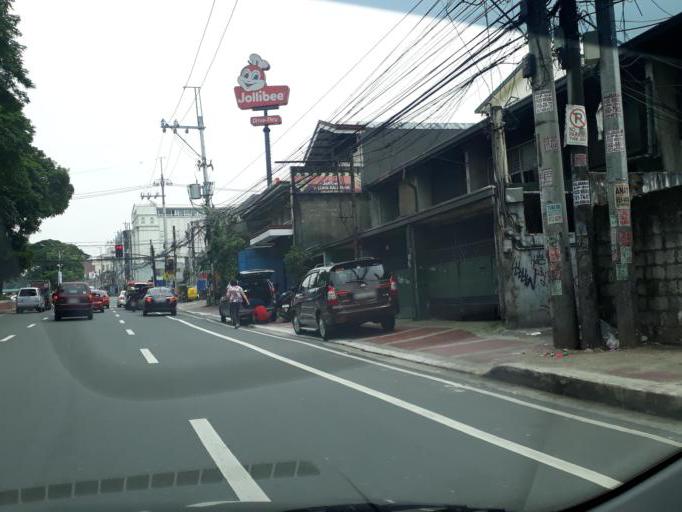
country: PH
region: Metro Manila
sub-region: Quezon City
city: Quezon City
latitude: 14.6356
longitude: 121.0546
